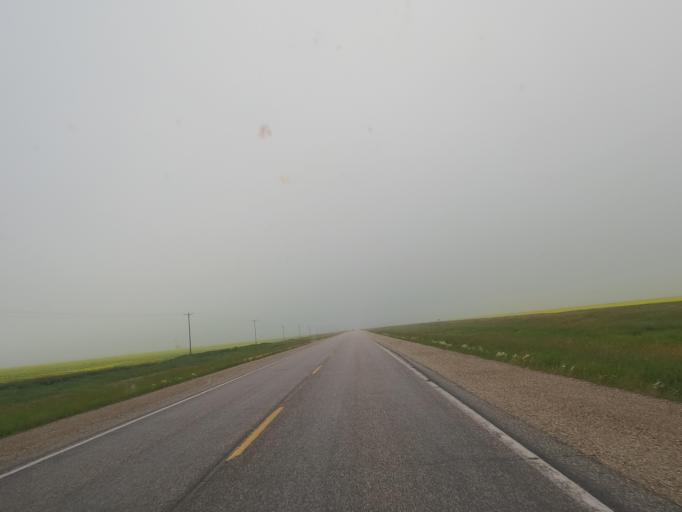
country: CA
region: Manitoba
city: Carman
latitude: 49.7068
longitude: -97.9287
